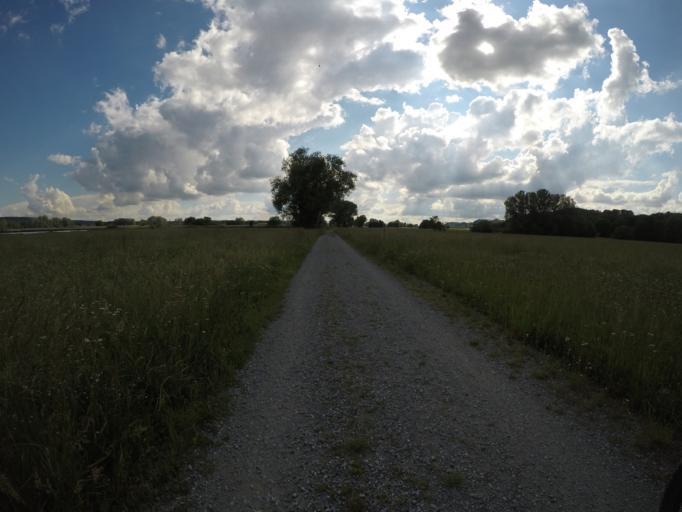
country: DE
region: Bavaria
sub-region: Lower Bavaria
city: Marklkofen
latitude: 48.5685
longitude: 12.5763
